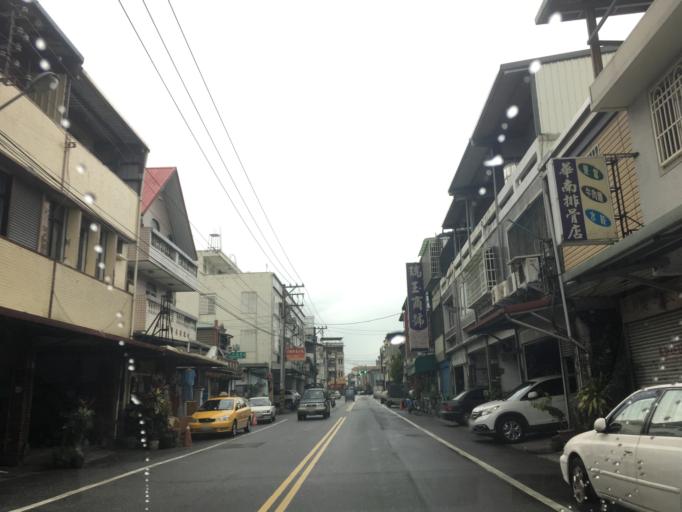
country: TW
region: Taiwan
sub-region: Hualien
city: Hualian
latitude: 23.9709
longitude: 121.5804
